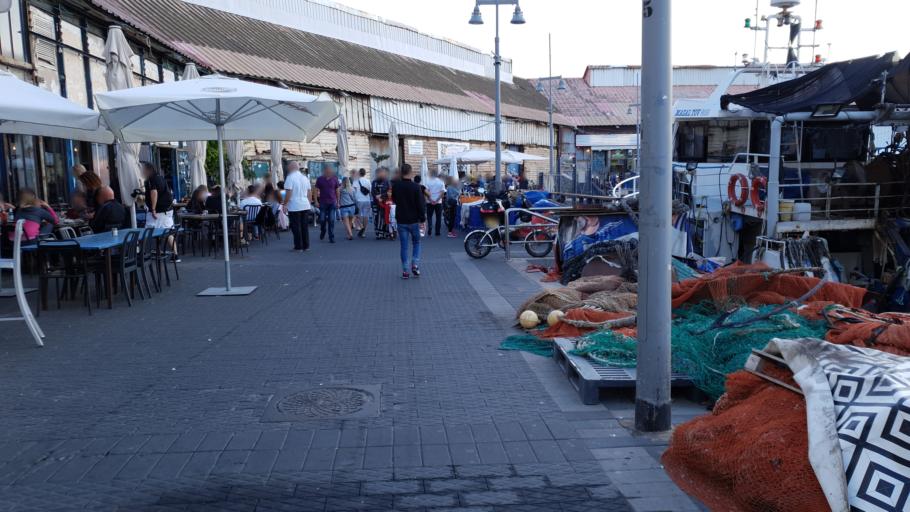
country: IL
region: Tel Aviv
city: Yafo
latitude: 32.0521
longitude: 34.7497
